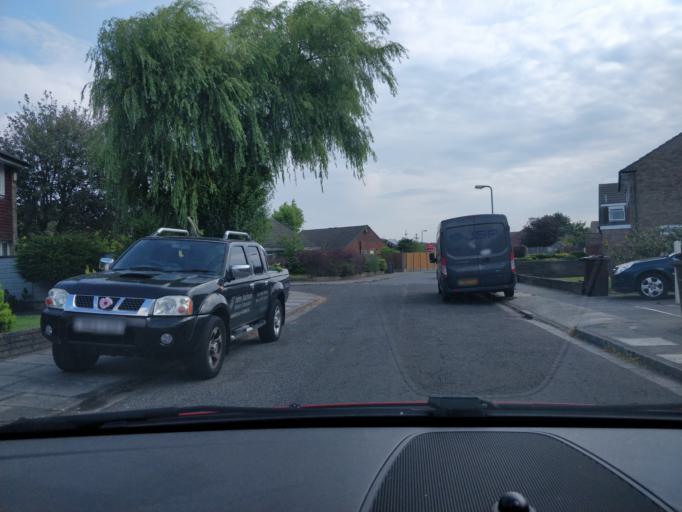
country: GB
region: England
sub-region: Sefton
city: Southport
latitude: 53.6745
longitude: -2.9666
